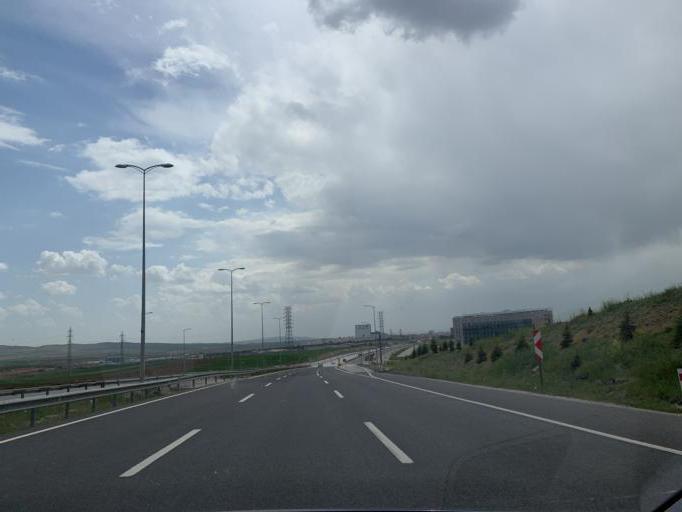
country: TR
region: Ankara
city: Polatli
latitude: 39.5925
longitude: 32.1727
